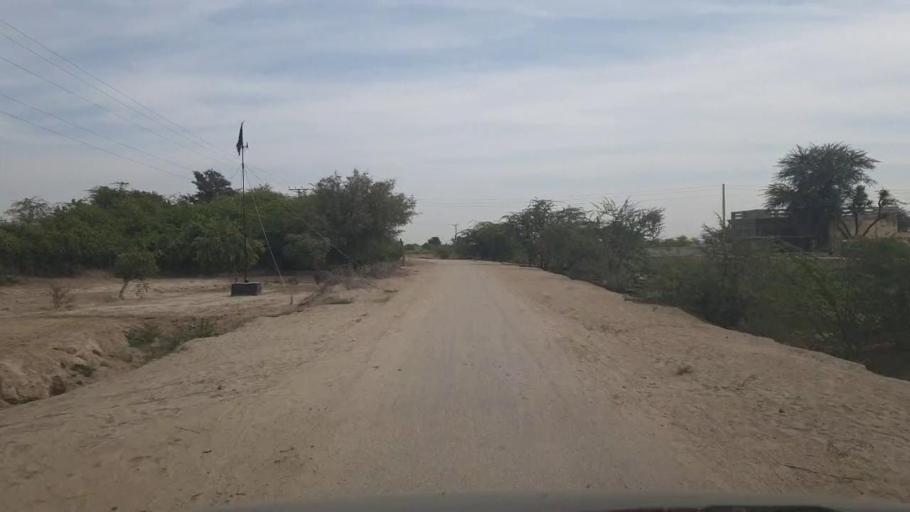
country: PK
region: Sindh
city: Kunri
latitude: 25.2526
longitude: 69.6290
